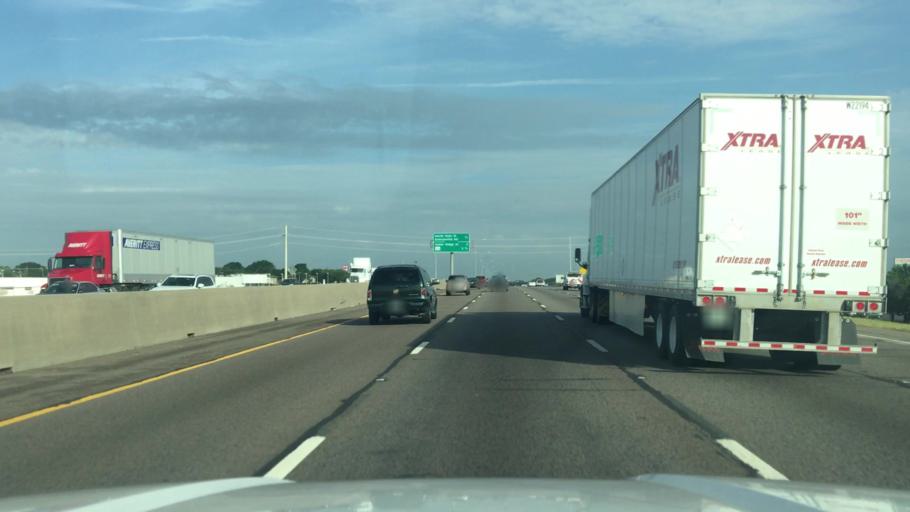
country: US
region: Texas
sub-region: Dallas County
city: Duncanville
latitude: 32.6592
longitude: -96.8892
